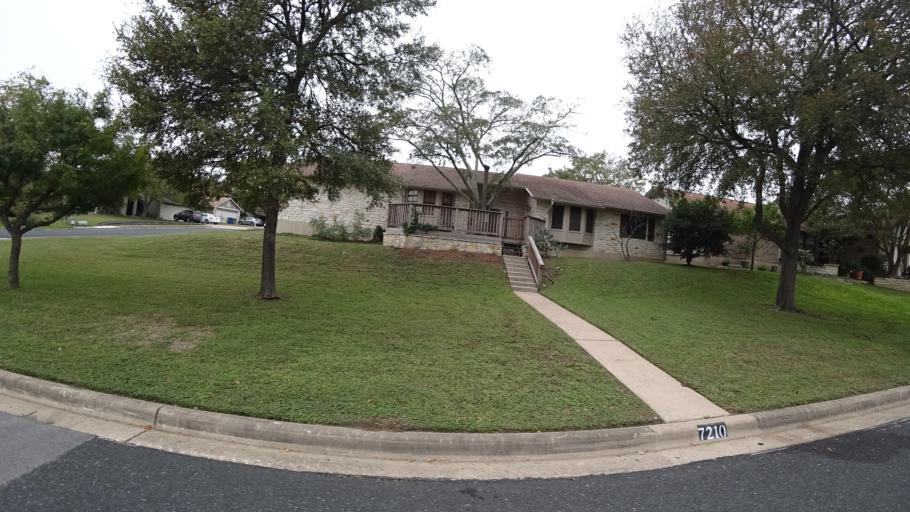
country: US
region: Texas
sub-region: Travis County
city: Barton Creek
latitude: 30.2401
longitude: -97.8946
